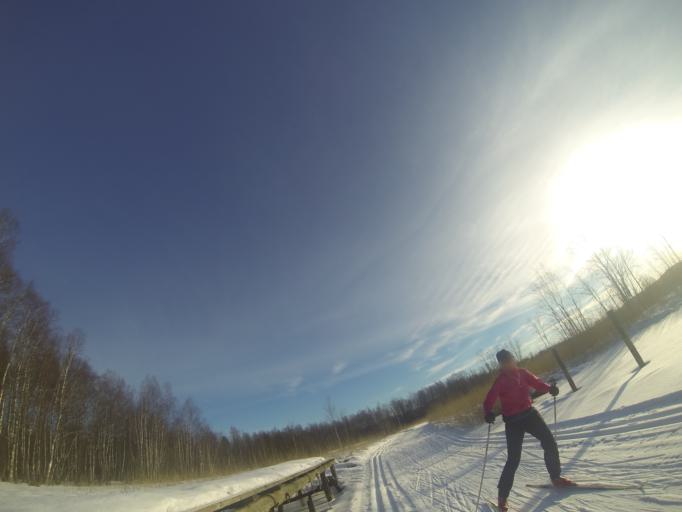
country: FI
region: Southern Savonia
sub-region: Savonlinna
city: Savonlinna
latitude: 61.9117
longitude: 28.9190
